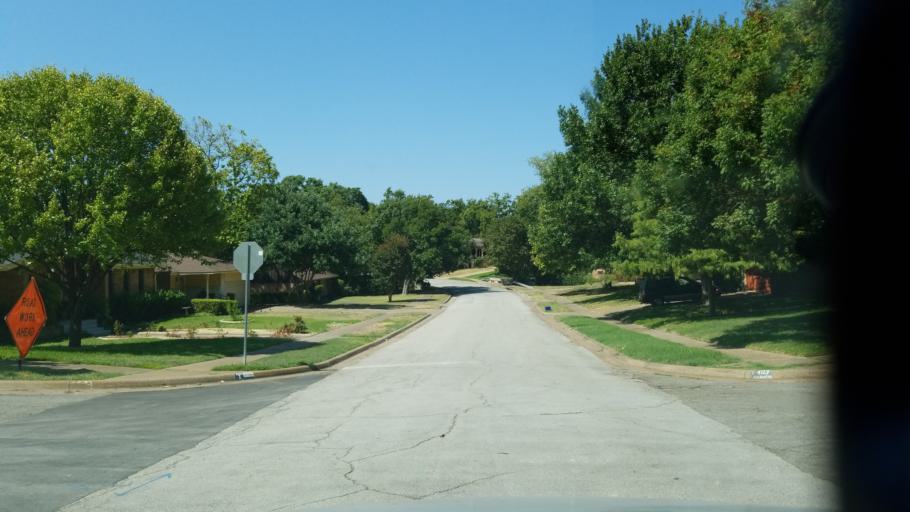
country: US
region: Texas
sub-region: Dallas County
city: Duncanville
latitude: 32.6502
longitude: -96.8976
